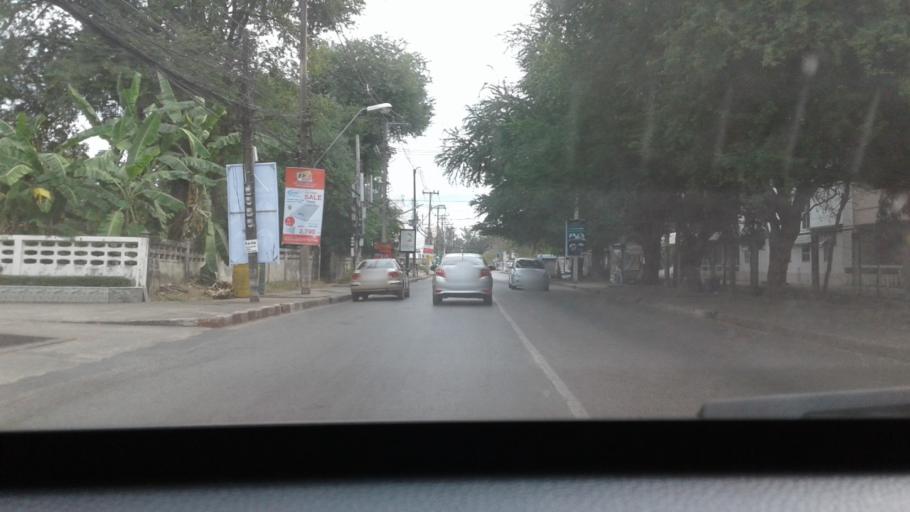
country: TH
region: Changwat Udon Thani
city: Udon Thani
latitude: 17.4182
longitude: 102.7874
